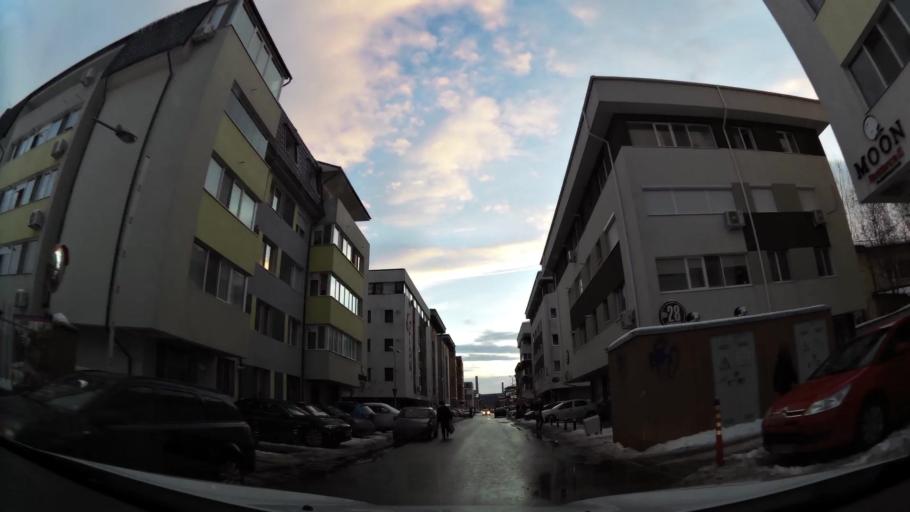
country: RO
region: Ilfov
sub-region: Comuna Popesti-Leordeni
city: Popesti-Leordeni
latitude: 44.3741
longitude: 26.1506
